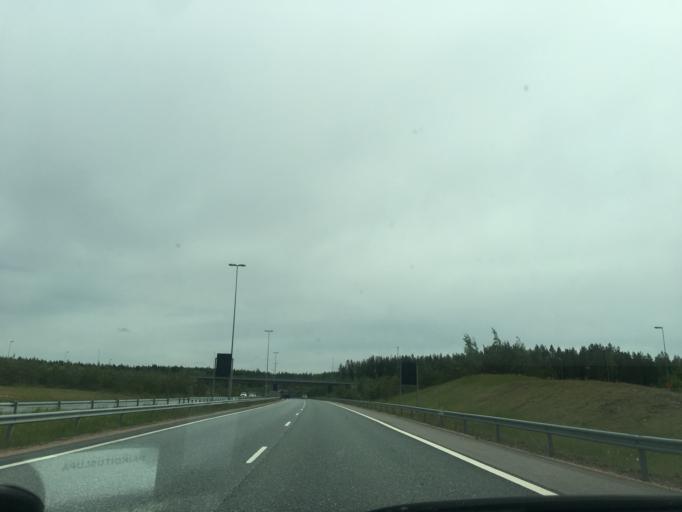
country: FI
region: Uusimaa
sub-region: Helsinki
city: Saukkola
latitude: 60.3441
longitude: 23.9087
